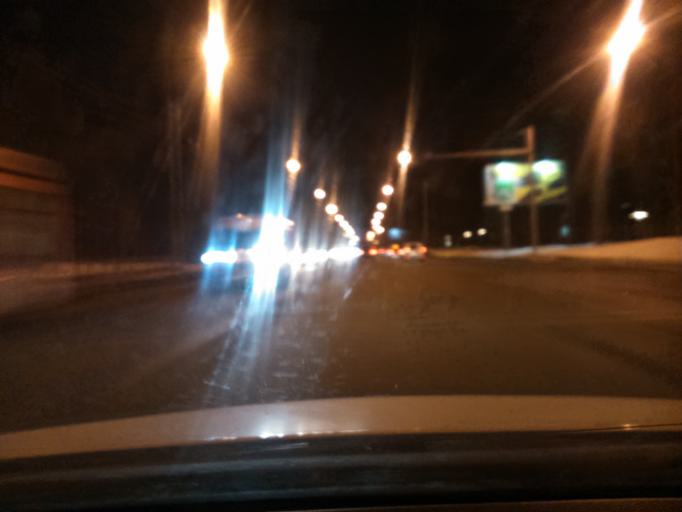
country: RU
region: Perm
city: Perm
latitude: 57.9921
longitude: 56.1821
